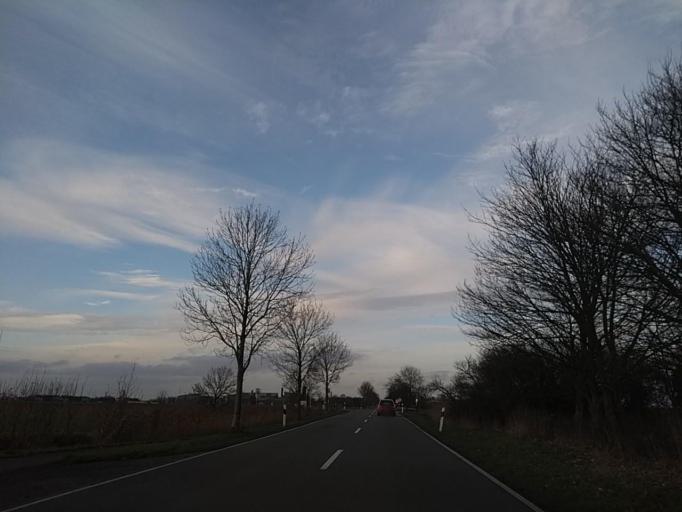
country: DE
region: Lower Saxony
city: Jemgum
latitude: 53.2437
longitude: 7.3910
